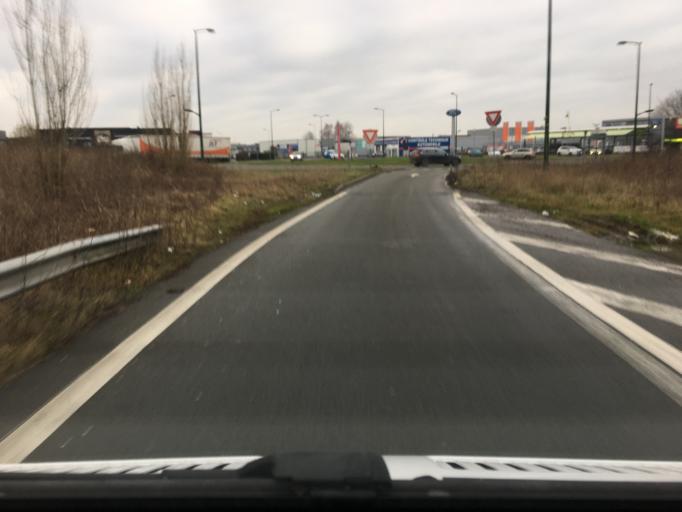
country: FR
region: Nord-Pas-de-Calais
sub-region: Departement du Nord
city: Bois-Grenier
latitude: 50.6590
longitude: 2.8914
